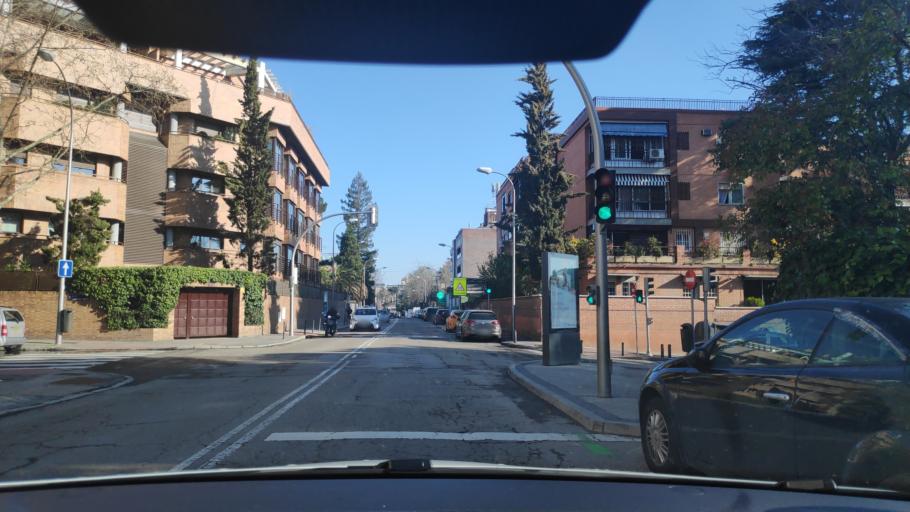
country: ES
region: Madrid
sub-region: Provincia de Madrid
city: Chamartin
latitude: 40.4642
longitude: -3.6798
